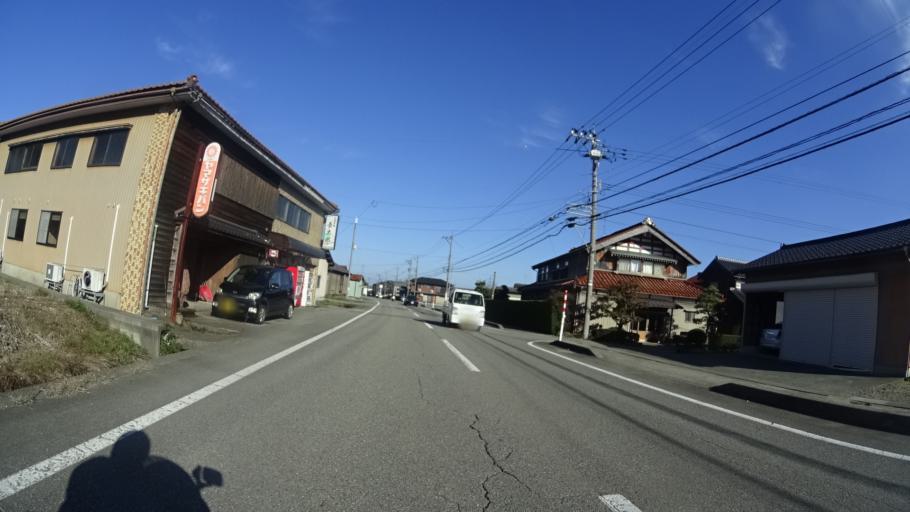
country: JP
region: Ishikawa
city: Komatsu
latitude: 36.2767
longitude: 136.3926
